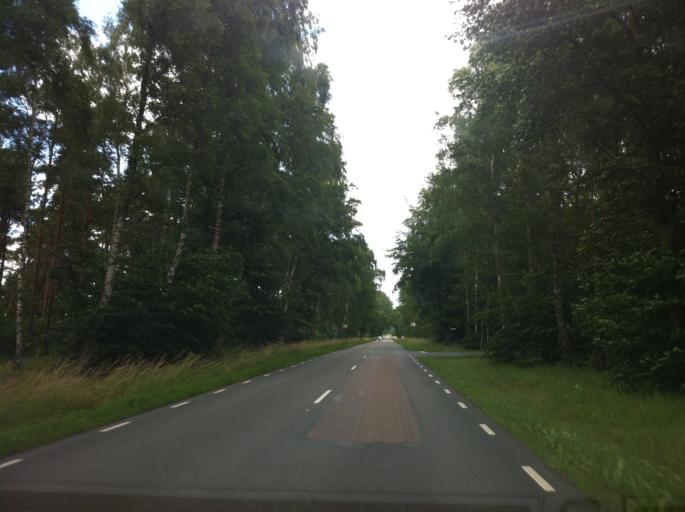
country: SE
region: Skane
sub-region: Simrishamns Kommun
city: Simrishamn
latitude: 55.4122
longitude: 14.1980
